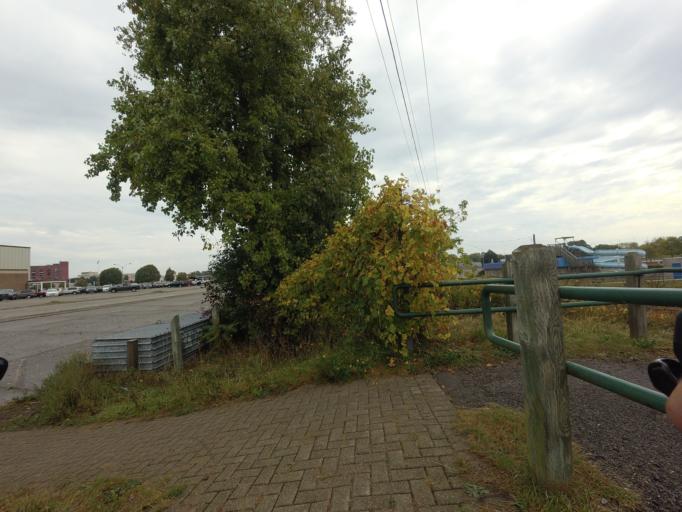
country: CA
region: Ontario
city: Brantford
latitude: 43.1343
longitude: -80.2653
